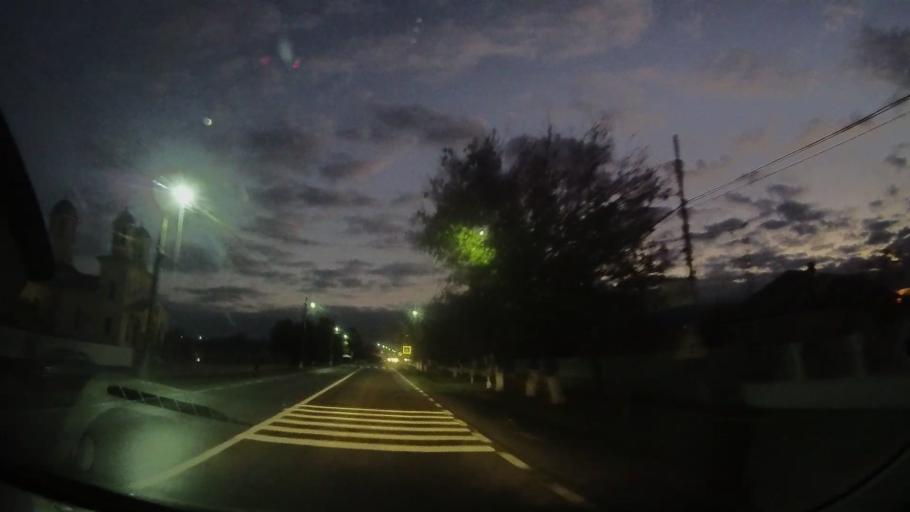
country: RO
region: Tulcea
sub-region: Comuna Mihail Kogalniceanu
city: Mihail Kogalniceanu
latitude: 45.0408
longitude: 28.7349
